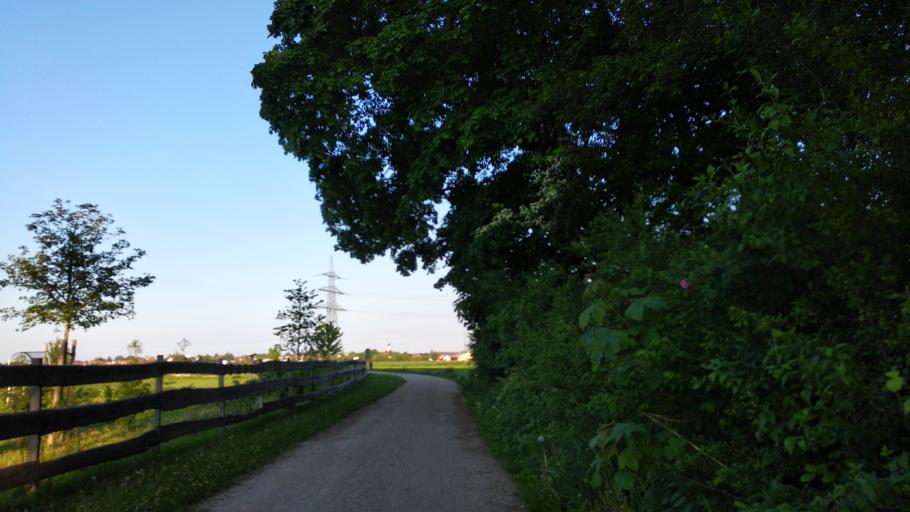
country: DE
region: Bavaria
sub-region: Upper Bavaria
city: Zorneding
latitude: 48.0895
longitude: 11.8042
